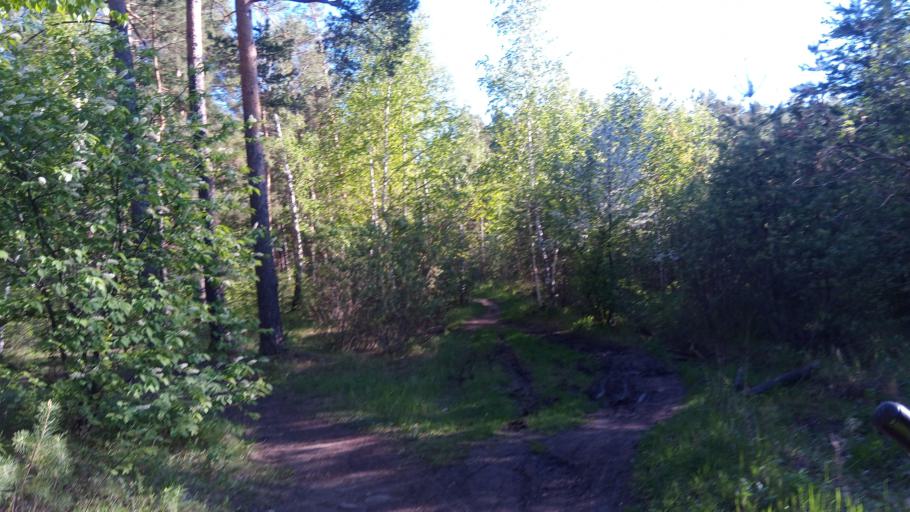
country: RU
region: Chelyabinsk
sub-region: Gorod Chelyabinsk
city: Chelyabinsk
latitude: 55.1379
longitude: 61.3378
